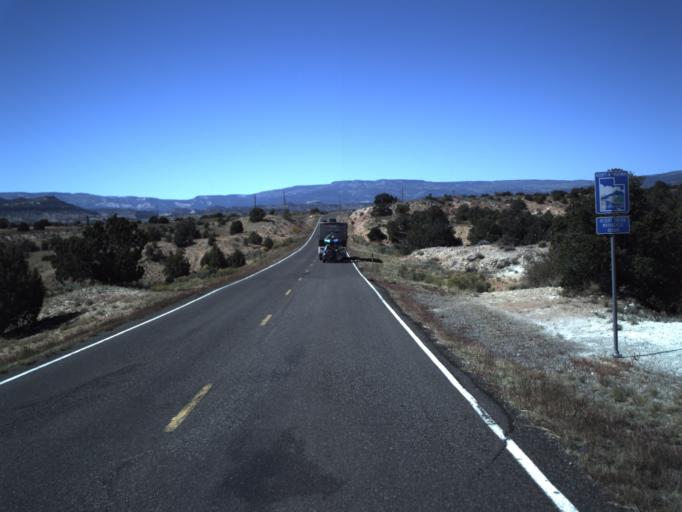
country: US
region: Utah
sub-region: Wayne County
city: Loa
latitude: 37.7404
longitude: -111.5537
